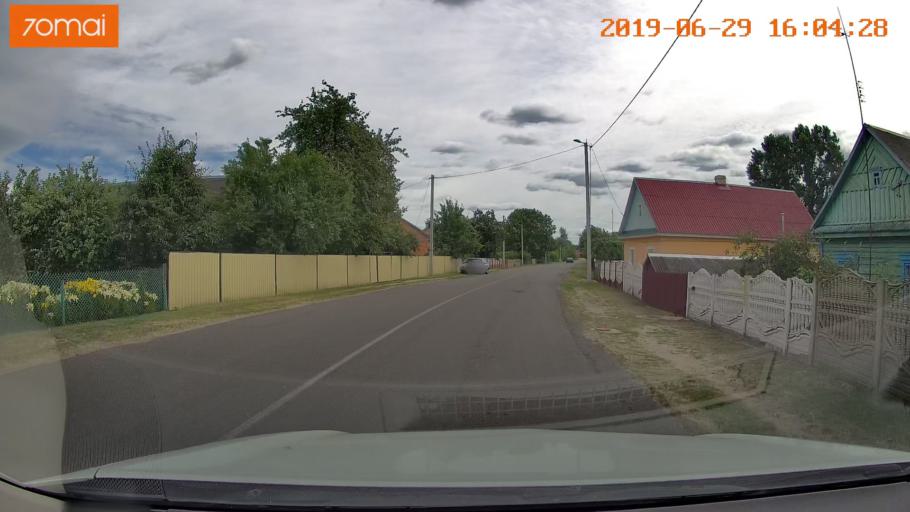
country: BY
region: Brest
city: Luninyets
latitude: 52.2224
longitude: 27.0250
